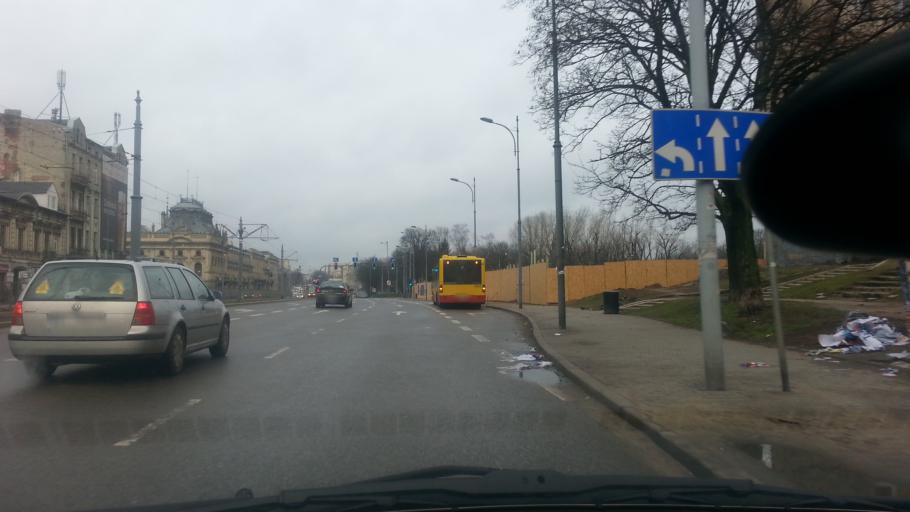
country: PL
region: Lodz Voivodeship
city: Lodz
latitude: 51.7772
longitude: 19.4521
